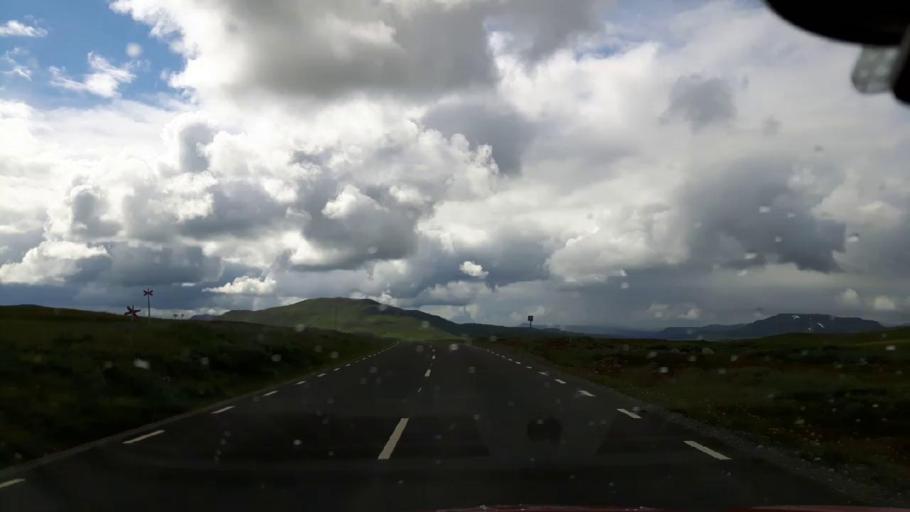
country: NO
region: Nordland
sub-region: Hattfjelldal
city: Hattfjelldal
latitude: 65.0446
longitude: 14.3316
